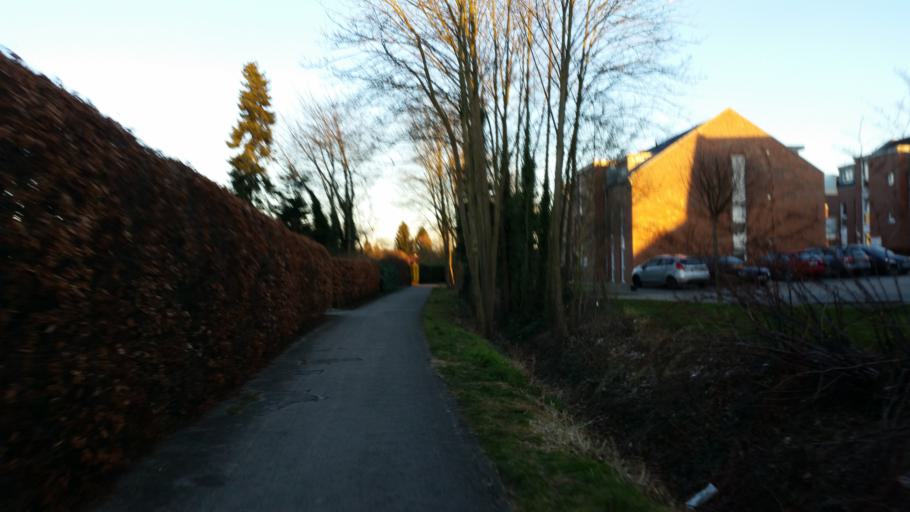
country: DE
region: North Rhine-Westphalia
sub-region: Regierungsbezirk Munster
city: Rheine
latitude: 52.2819
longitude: 7.4202
